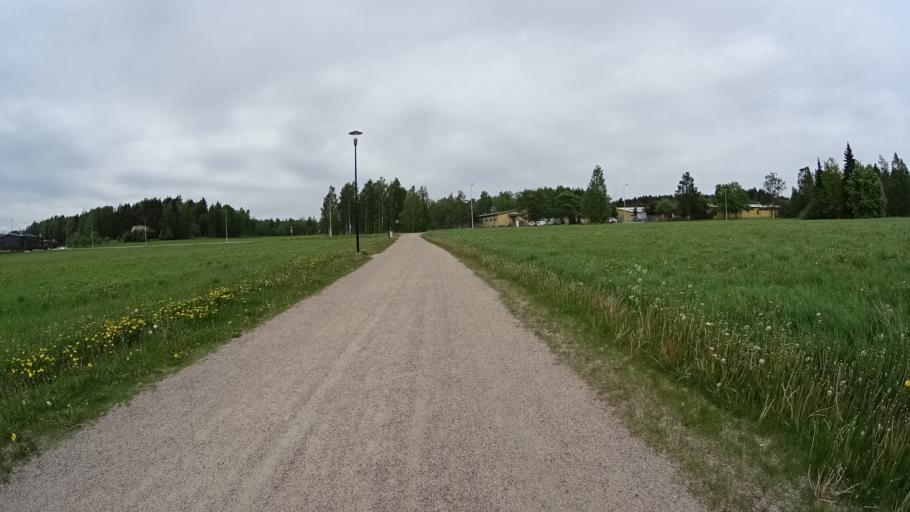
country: FI
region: Uusimaa
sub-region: Helsinki
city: Vantaa
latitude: 60.3007
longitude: 25.0128
